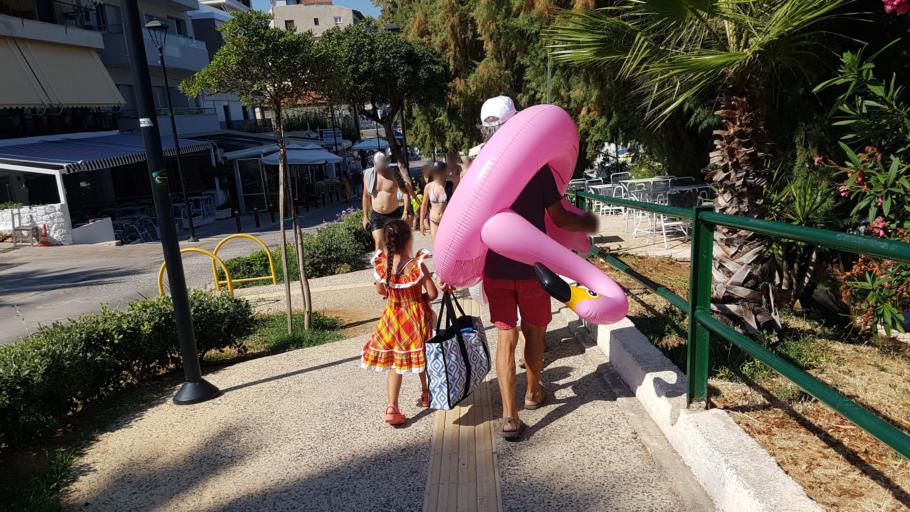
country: GR
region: Crete
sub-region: Nomos Chanias
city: Chania
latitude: 35.5157
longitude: 24.0089
